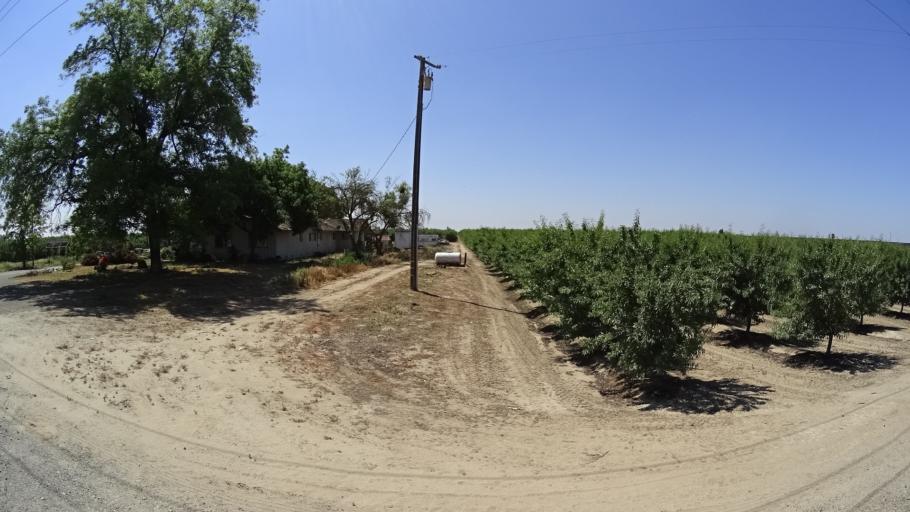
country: US
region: California
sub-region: Fresno County
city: Kingsburg
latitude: 36.4888
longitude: -119.5769
